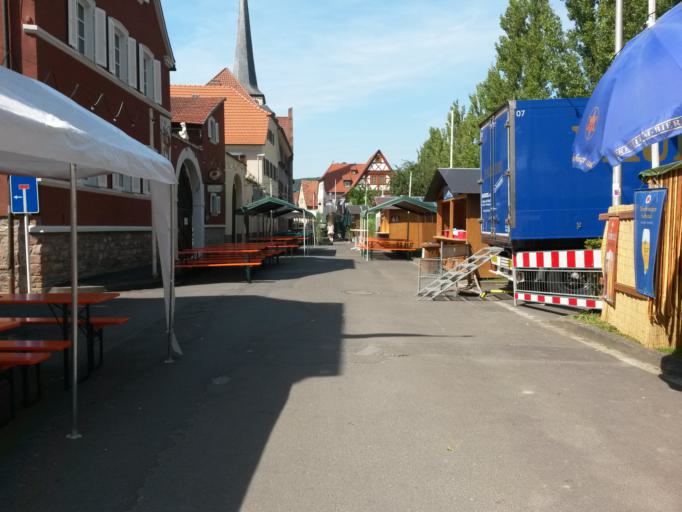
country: DE
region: Bavaria
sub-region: Regierungsbezirk Unterfranken
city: Margetshochheim
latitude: 49.8366
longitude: 9.8666
